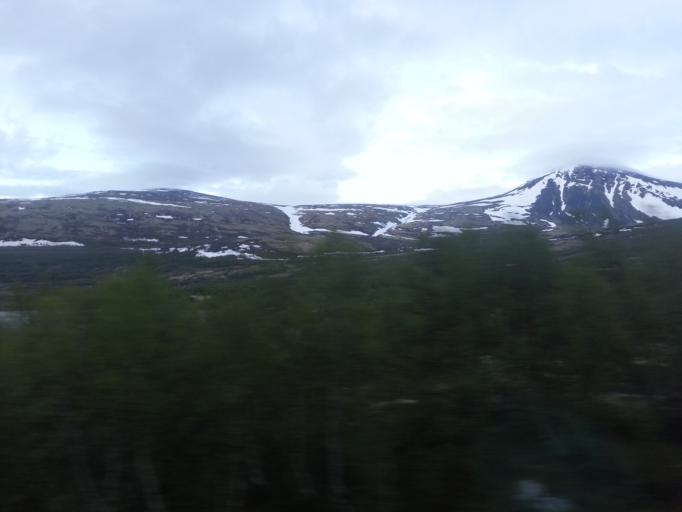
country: NO
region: Oppland
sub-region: Dovre
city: Dovre
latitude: 62.1757
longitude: 9.4455
